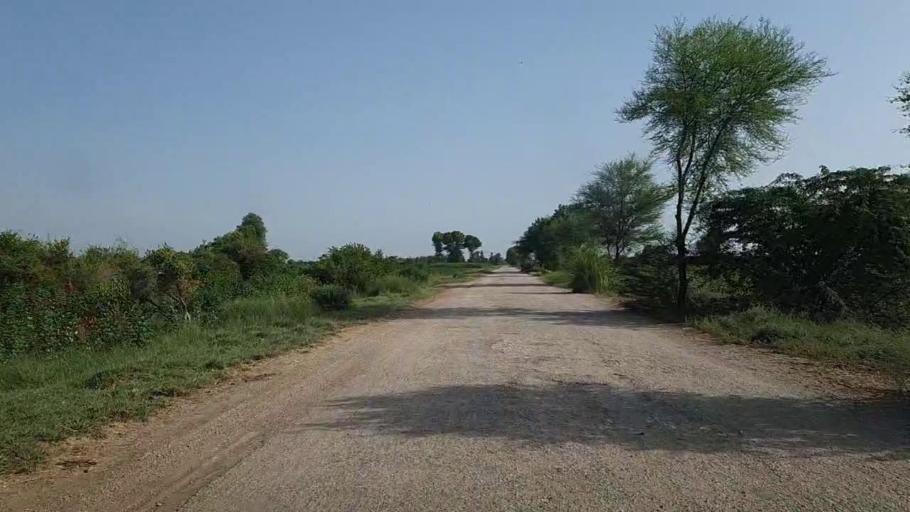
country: PK
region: Sindh
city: Karaundi
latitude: 26.8669
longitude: 68.3308
